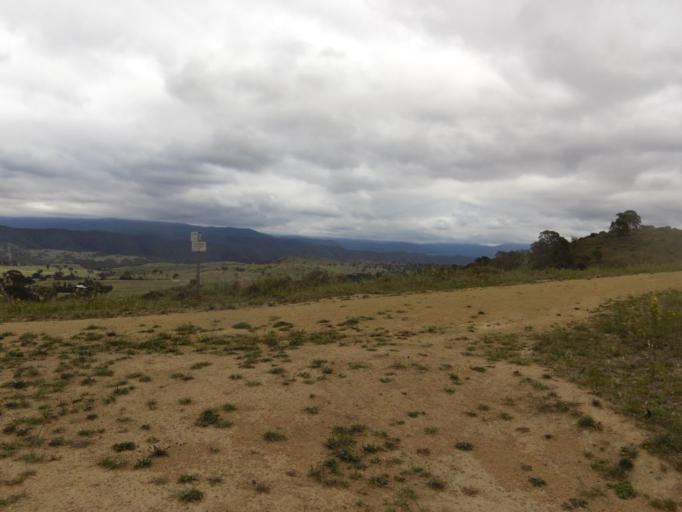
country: AU
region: Australian Capital Territory
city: Macarthur
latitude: -35.3662
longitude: 149.0413
